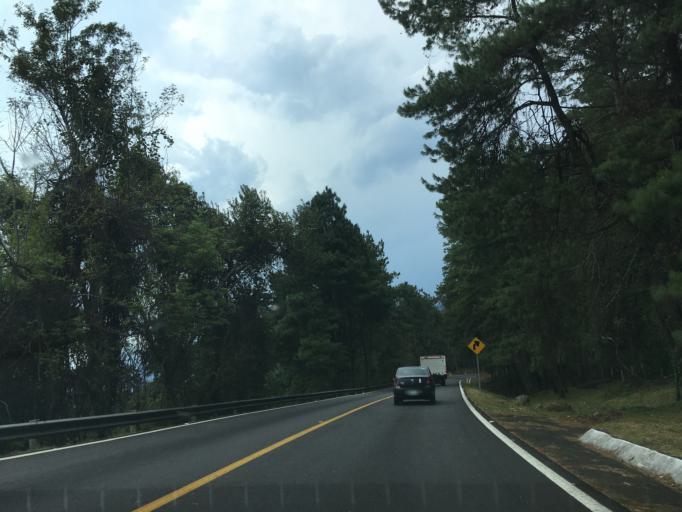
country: MX
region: Michoacan
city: Tingambato
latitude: 19.4994
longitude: -101.8299
